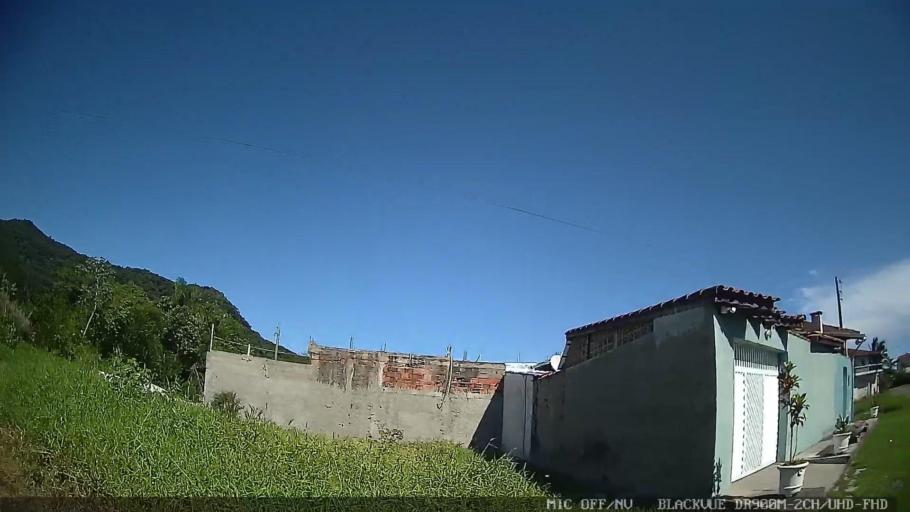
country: BR
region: Sao Paulo
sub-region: Iguape
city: Iguape
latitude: -24.6910
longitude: -47.5616
